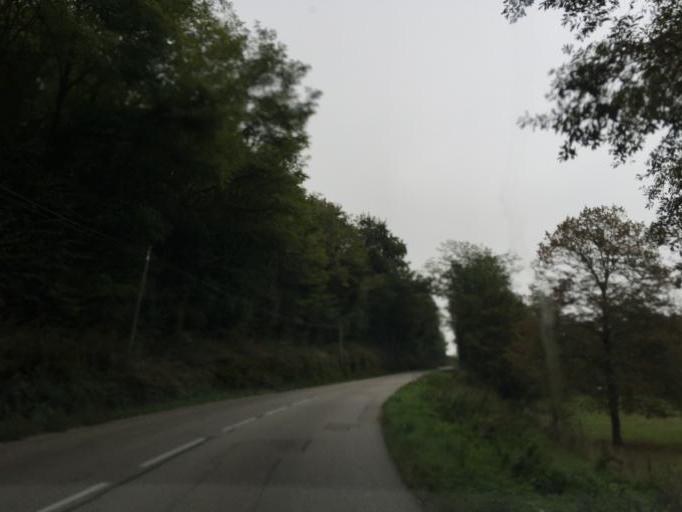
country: FR
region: Rhone-Alpes
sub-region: Departement de l'Isere
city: Saint-Clair-de-la-Tour
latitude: 45.5777
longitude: 5.4818
